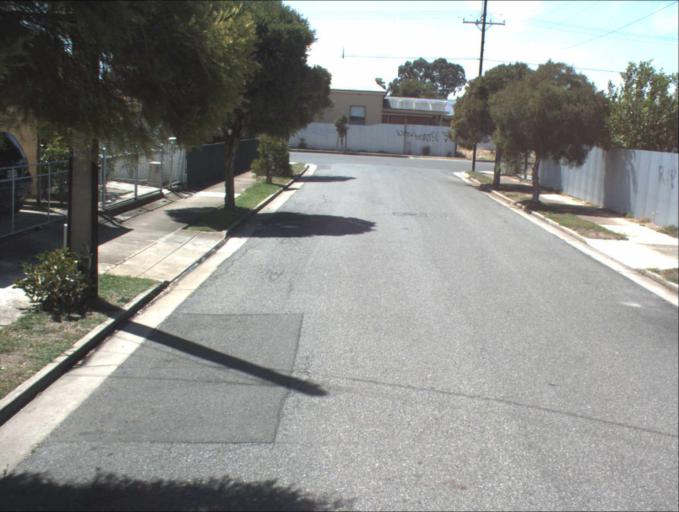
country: AU
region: South Australia
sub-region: Port Adelaide Enfield
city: Alberton
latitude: -34.8550
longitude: 138.5232
